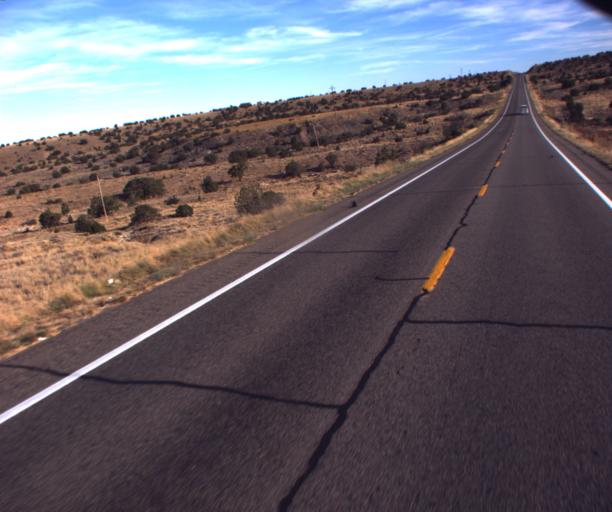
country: US
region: New Mexico
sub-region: San Juan County
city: Shiprock
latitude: 36.8863
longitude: -109.0555
